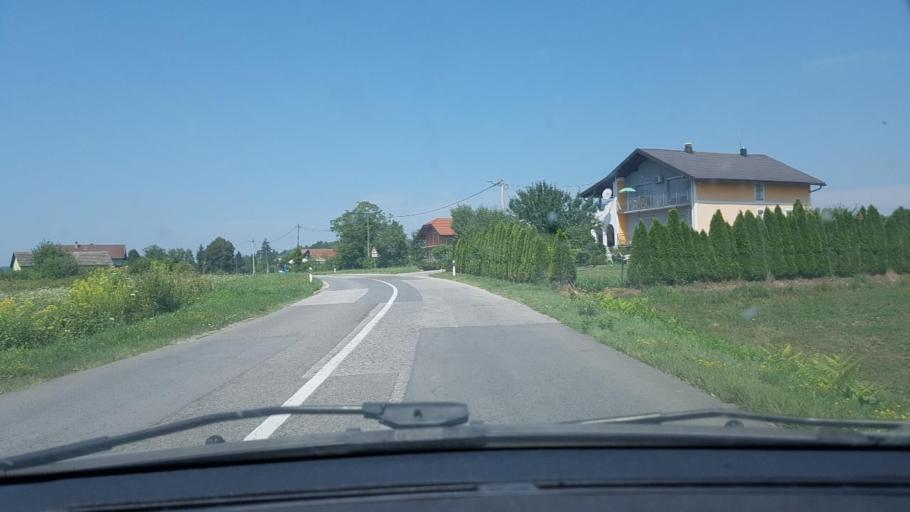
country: BA
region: Federation of Bosnia and Herzegovina
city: Velika Kladusa
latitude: 45.2153
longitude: 15.7601
